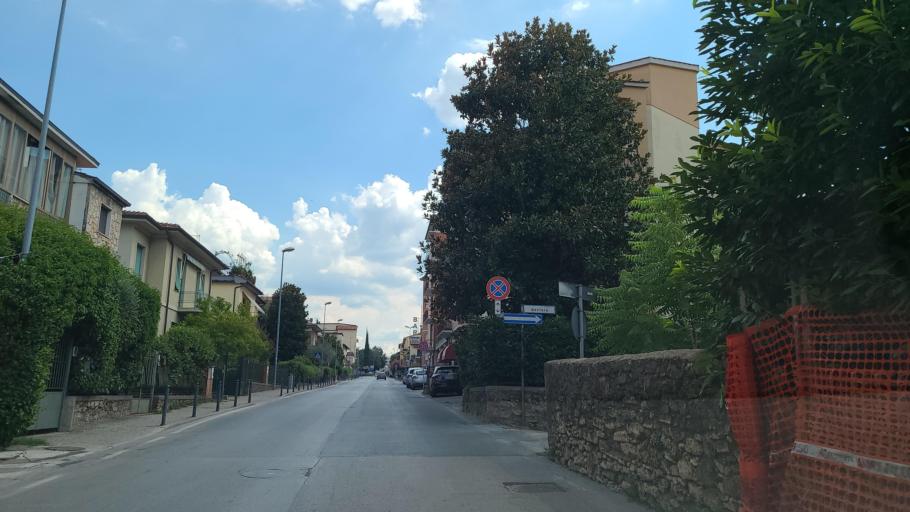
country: IT
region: Tuscany
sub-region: Provincia di Siena
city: Colle di Val d'Elsa
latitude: 43.4191
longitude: 11.1284
